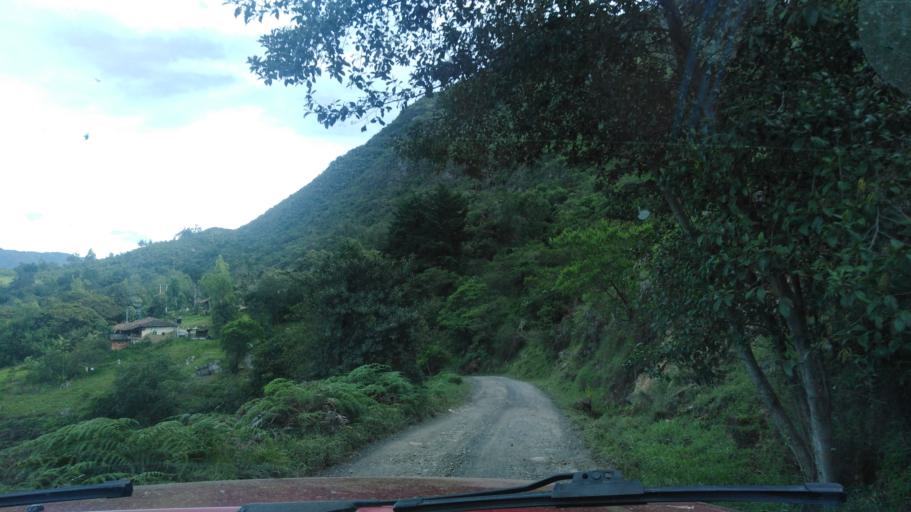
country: CO
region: Boyaca
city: San Mateo
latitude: 6.4369
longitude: -72.5730
